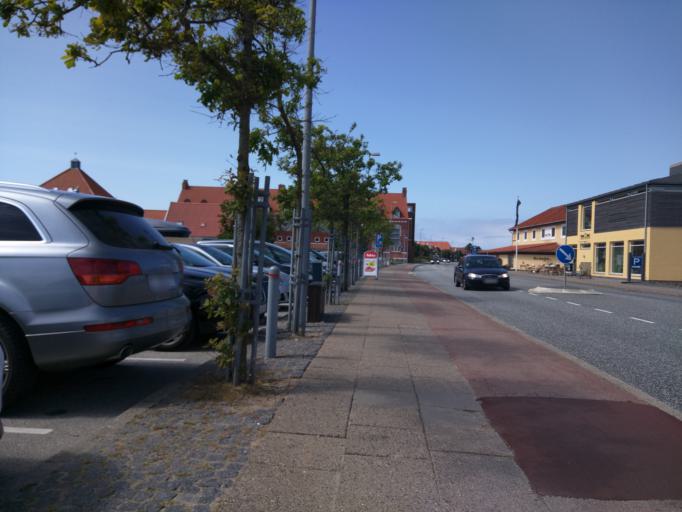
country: DK
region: North Denmark
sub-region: Frederikshavn Kommune
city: Skagen
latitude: 57.7233
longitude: 10.5891
